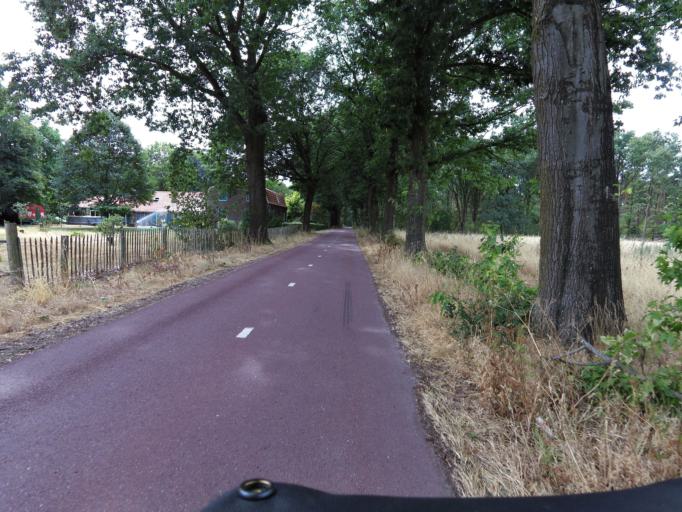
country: NL
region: Limburg
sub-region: Gemeente Venlo
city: Arcen
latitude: 51.5263
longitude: 6.1905
